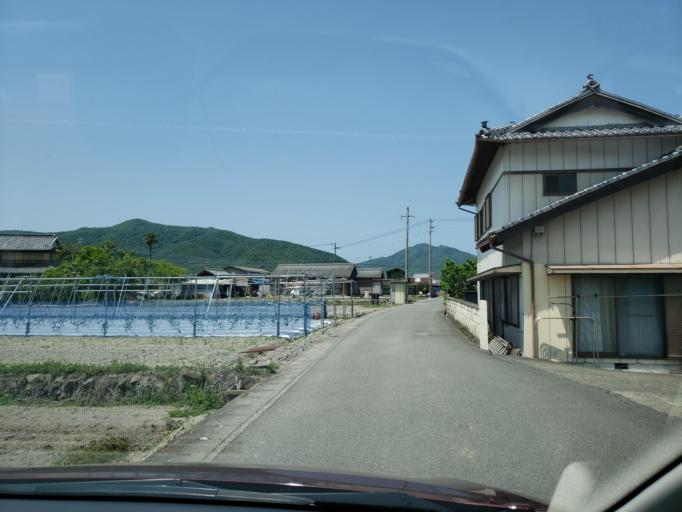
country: JP
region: Tokushima
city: Kamojimacho-jogejima
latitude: 34.0906
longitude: 134.2681
